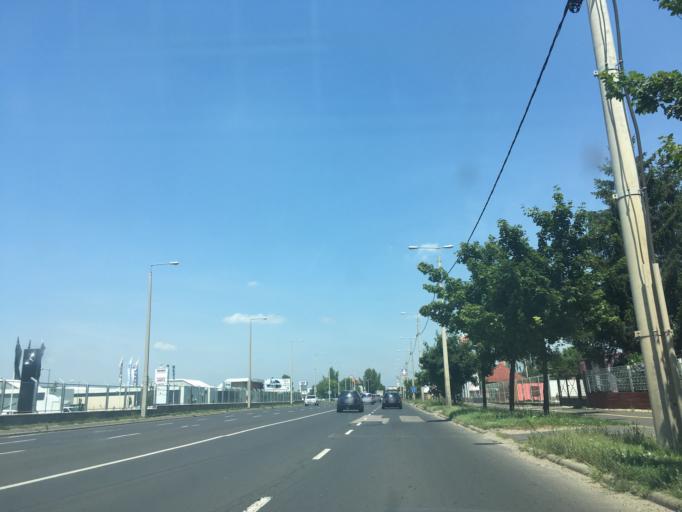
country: HU
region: Hajdu-Bihar
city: Debrecen
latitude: 47.5005
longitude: 21.6312
